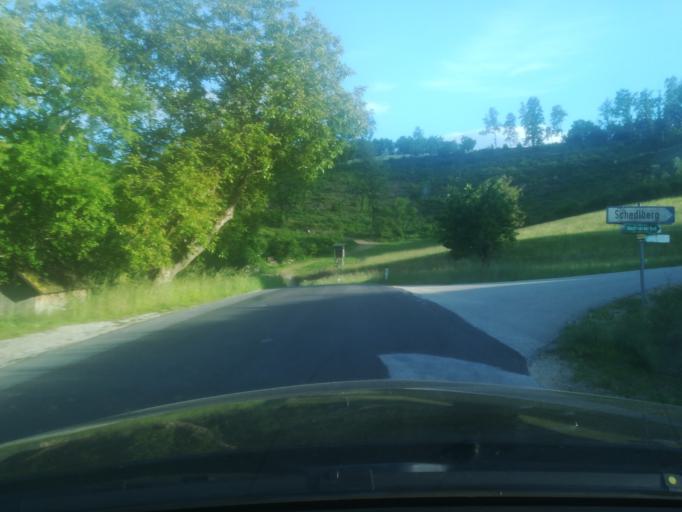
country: AT
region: Upper Austria
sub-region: Politischer Bezirk Perg
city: Perg
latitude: 48.3069
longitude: 14.6074
